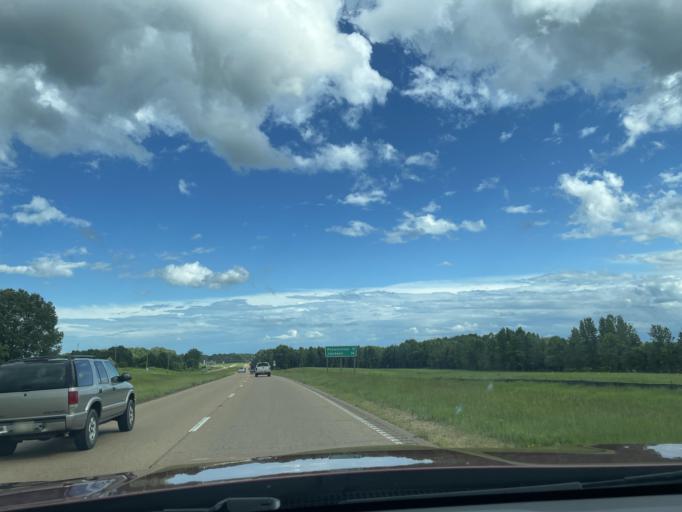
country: US
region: Mississippi
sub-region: Madison County
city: Flora
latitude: 32.5363
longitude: -90.3184
